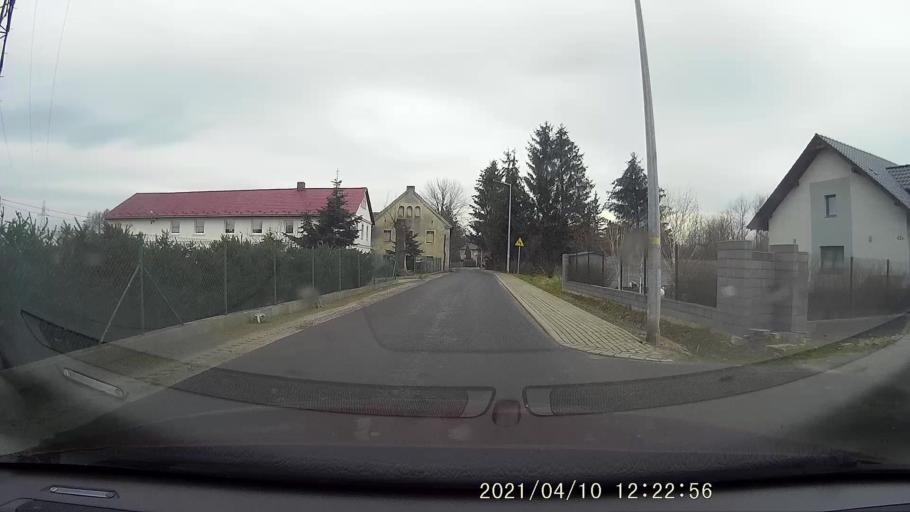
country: PL
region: Lower Silesian Voivodeship
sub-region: Powiat zgorzelecki
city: Lagow
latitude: 51.1656
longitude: 15.0383
